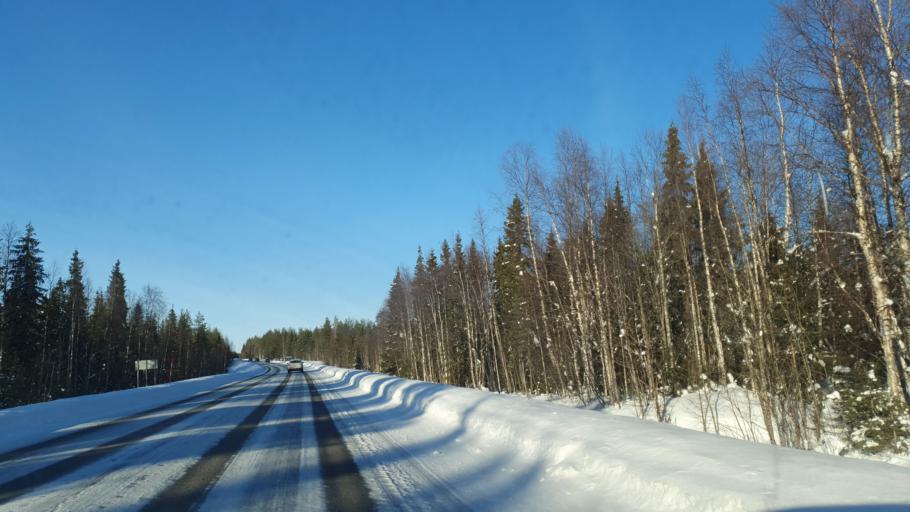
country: FI
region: Lapland
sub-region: Torniolaakso
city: Pello
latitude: 67.0328
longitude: 24.0354
